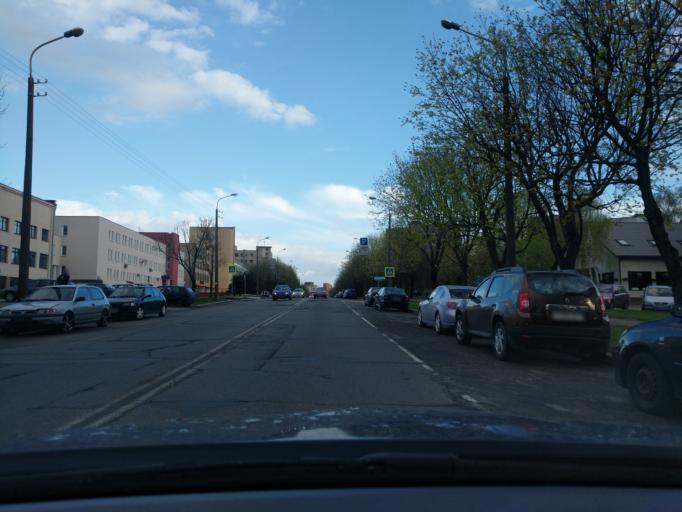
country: BY
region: Minsk
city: Novoye Medvezhino
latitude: 53.9159
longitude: 27.5035
